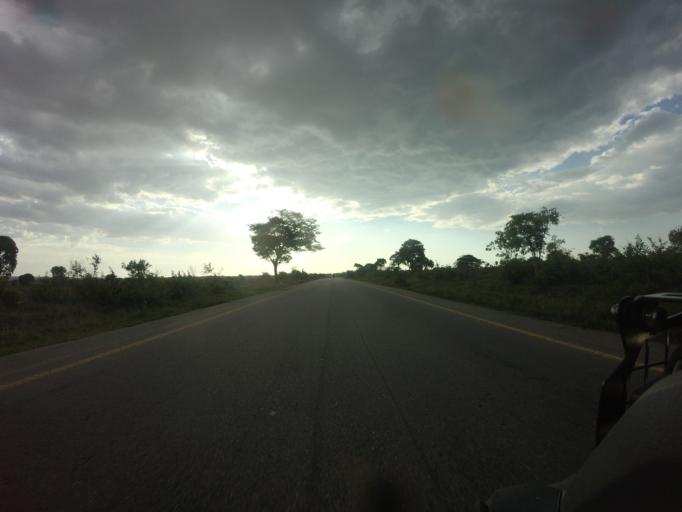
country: AO
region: Huila
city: Lubango
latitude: -14.6036
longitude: 14.0187
